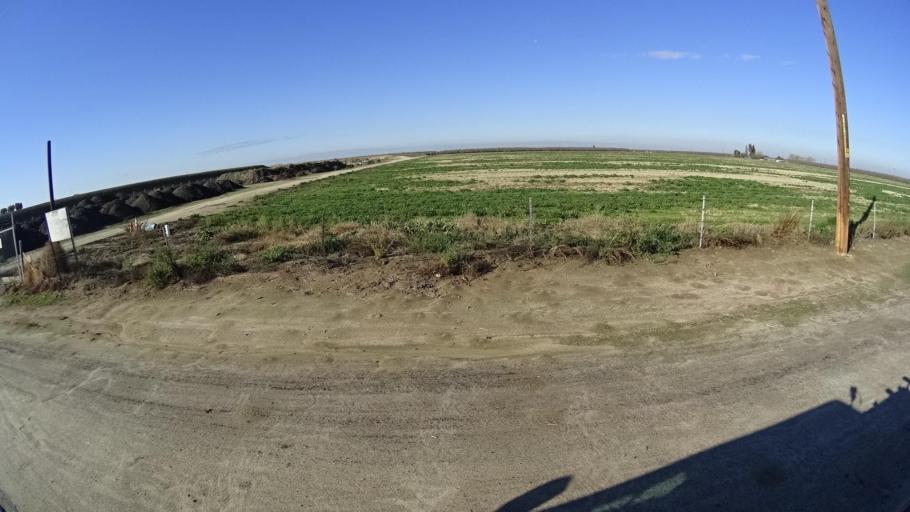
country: US
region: California
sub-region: Kern County
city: McFarland
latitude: 35.6855
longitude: -119.2765
